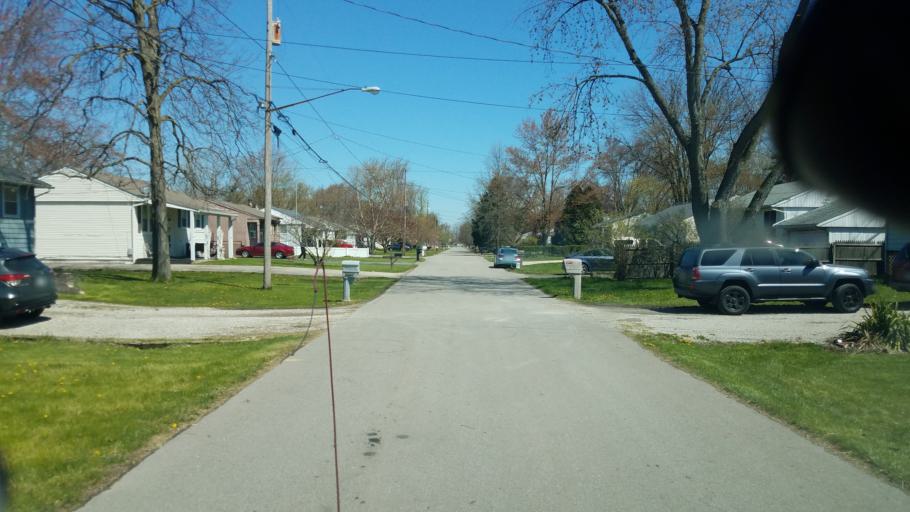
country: US
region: Ohio
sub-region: Marion County
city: Marion
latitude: 40.6362
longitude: -83.0790
